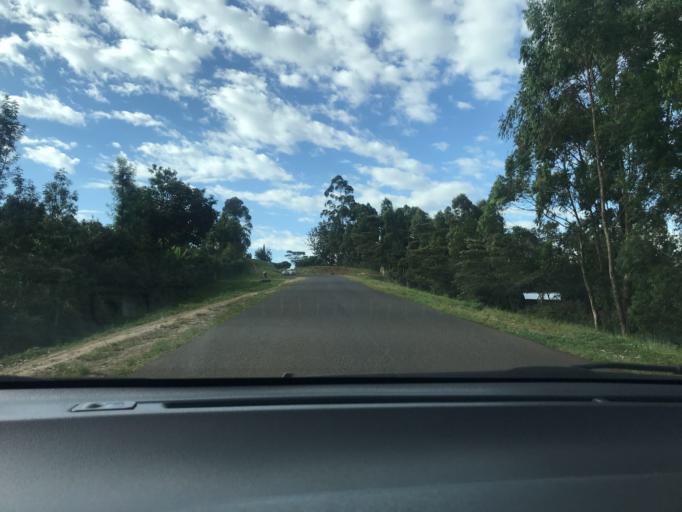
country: KE
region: Kirinyaga
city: Keruguya
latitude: -0.4865
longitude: 37.2052
